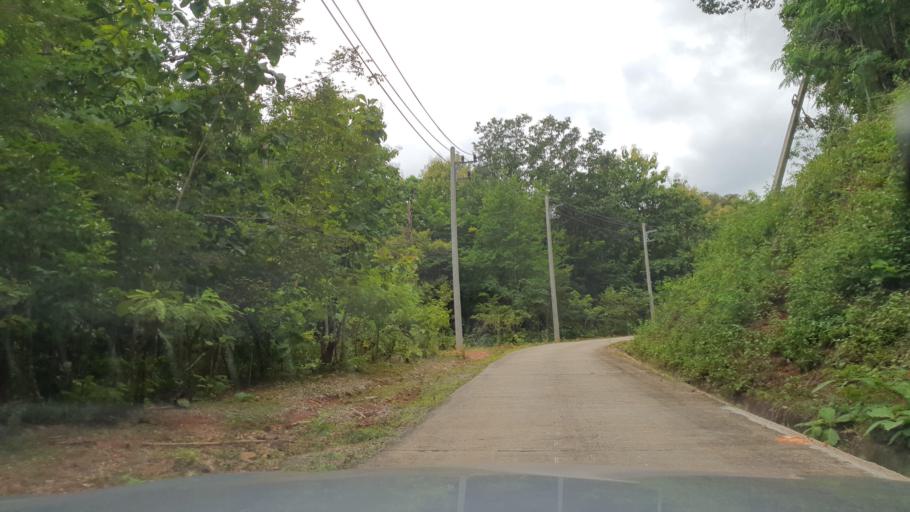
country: TH
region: Chiang Mai
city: Mae Wang
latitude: 18.6813
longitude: 98.6304
